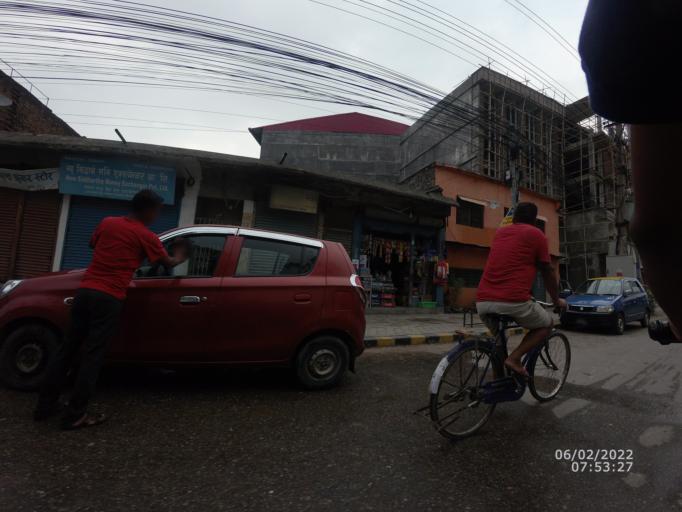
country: NP
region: Western Region
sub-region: Lumbini Zone
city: Bhairahawa
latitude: 27.5065
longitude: 83.4563
